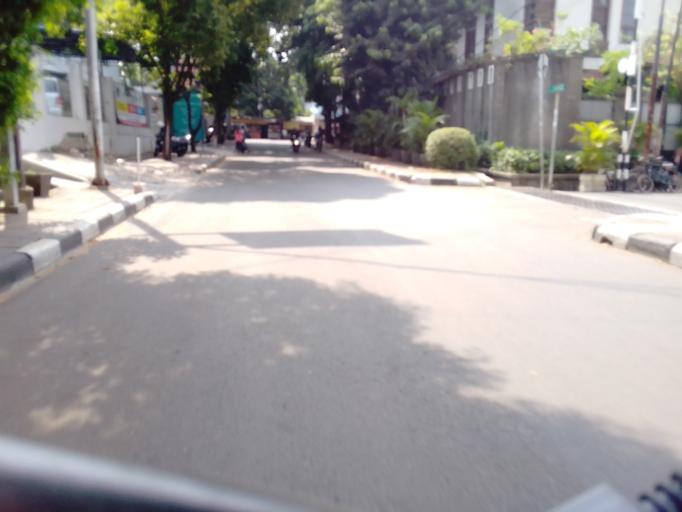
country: ID
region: Jakarta Raya
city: Jakarta
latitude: -6.2070
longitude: 106.8088
